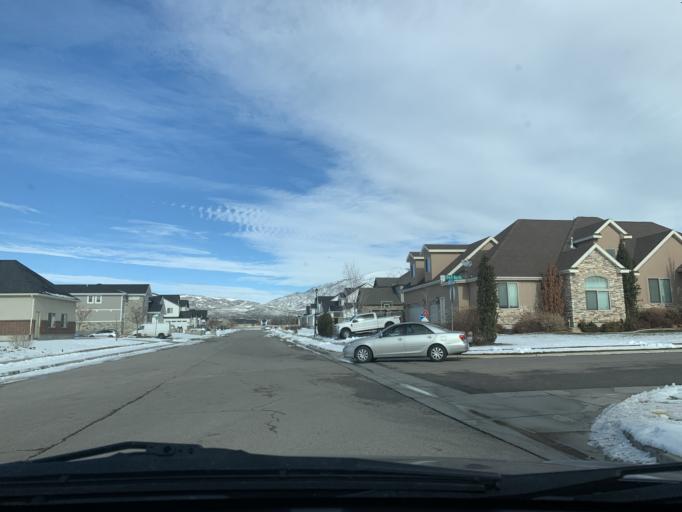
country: US
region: Utah
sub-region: Utah County
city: Lehi
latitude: 40.4117
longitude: -111.8226
